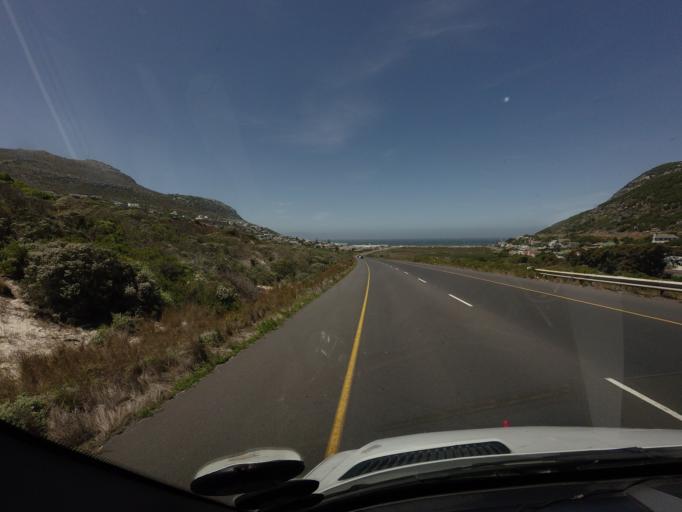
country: ZA
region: Western Cape
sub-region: City of Cape Town
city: Retreat
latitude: -34.1592
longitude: 18.4309
